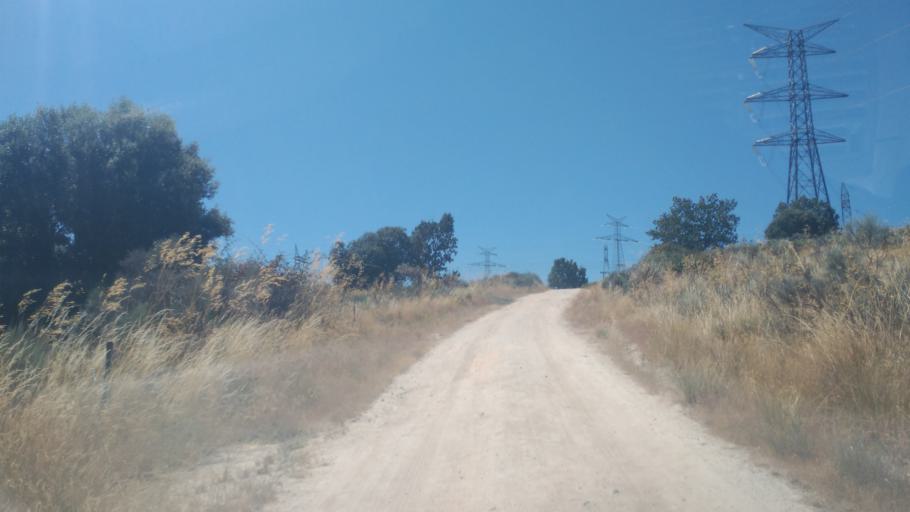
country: ES
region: Castille and Leon
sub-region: Provincia de Salamanca
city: Mieza
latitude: 41.2091
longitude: -6.6762
